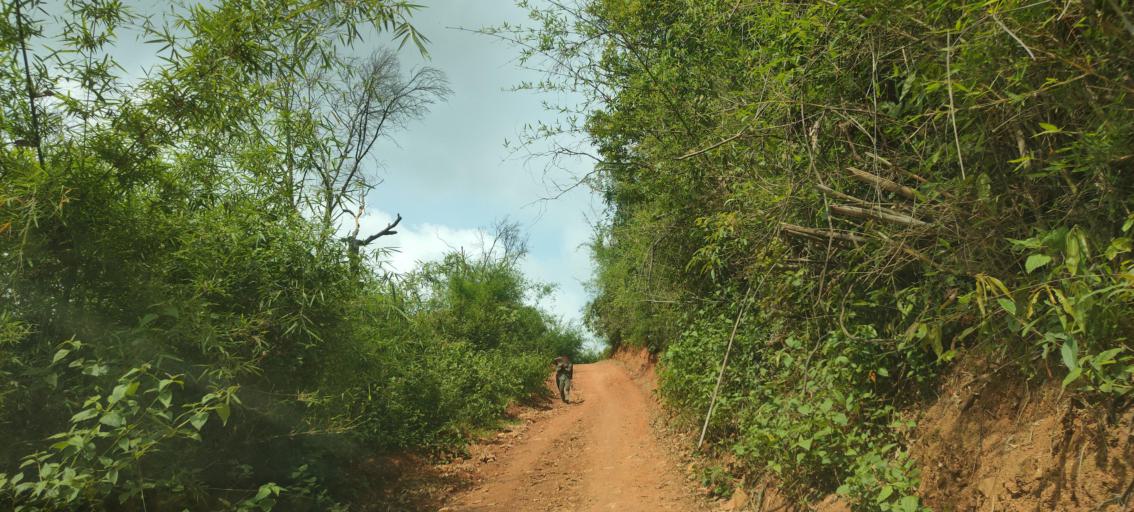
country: LA
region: Loungnamtha
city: Muang Nale
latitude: 20.4270
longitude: 101.4696
